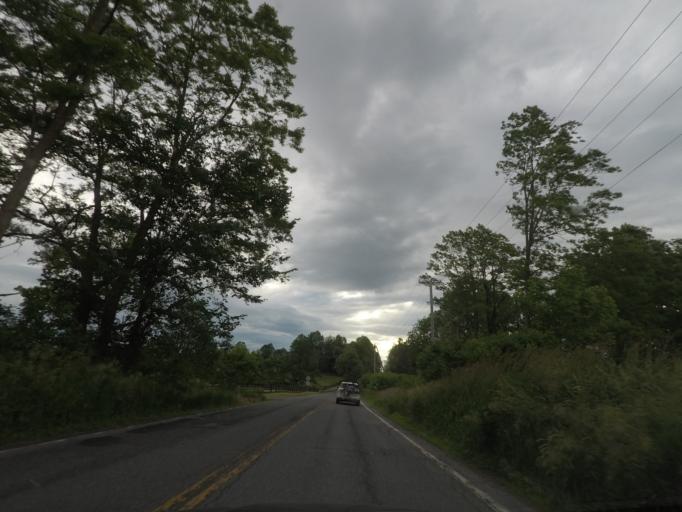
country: US
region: New York
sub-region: Dutchess County
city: Pine Plains
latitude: 41.9749
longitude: -73.6011
